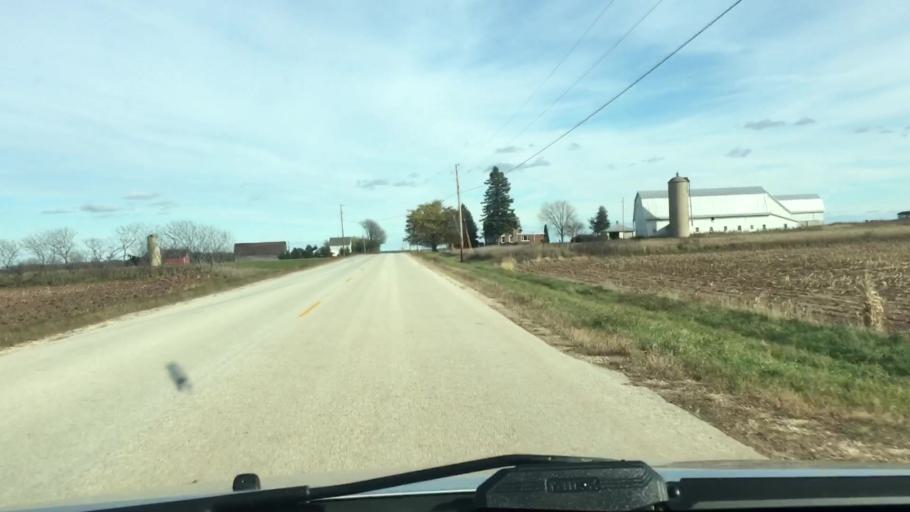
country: US
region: Wisconsin
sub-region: Kewaunee County
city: Algoma
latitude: 44.6974
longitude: -87.5910
